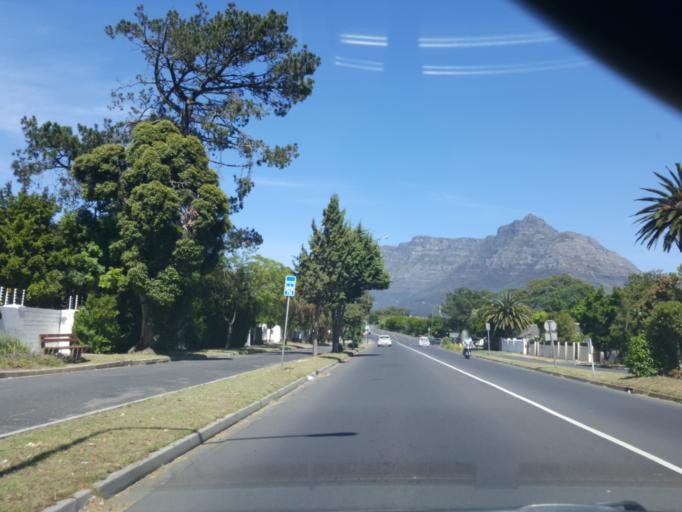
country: ZA
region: Western Cape
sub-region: City of Cape Town
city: Rosebank
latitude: -33.9437
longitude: 18.4944
